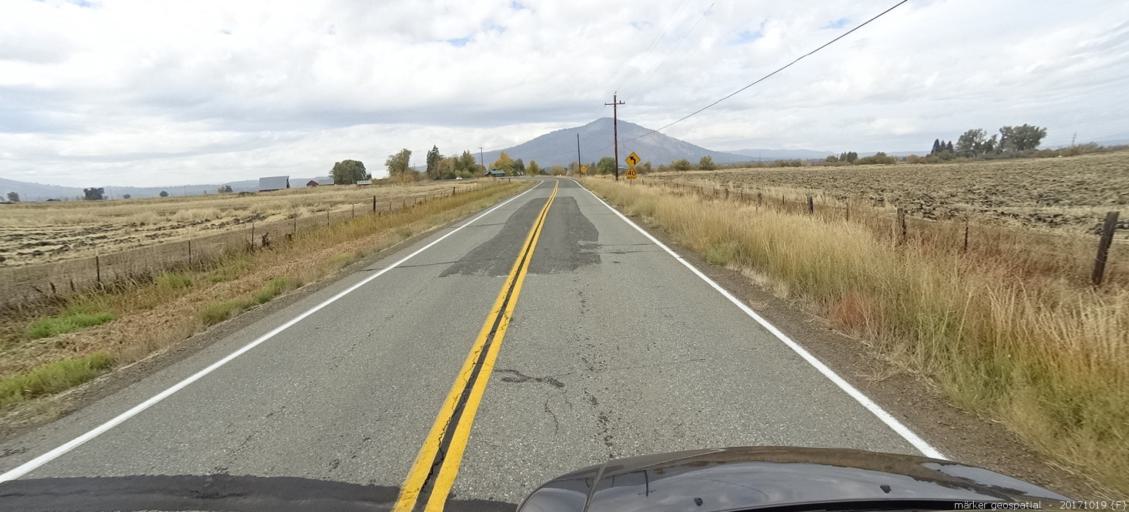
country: US
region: California
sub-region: Shasta County
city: Burney
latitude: 41.0624
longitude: -121.4782
